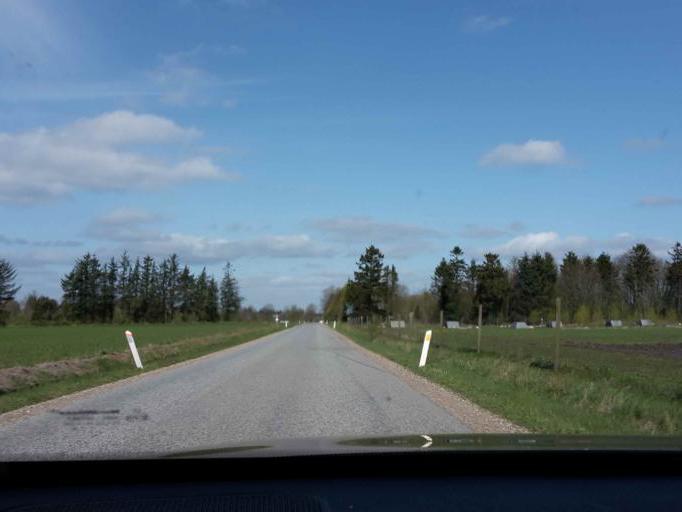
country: DK
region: South Denmark
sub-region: Vejen Kommune
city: Holsted
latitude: 55.5756
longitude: 8.9895
